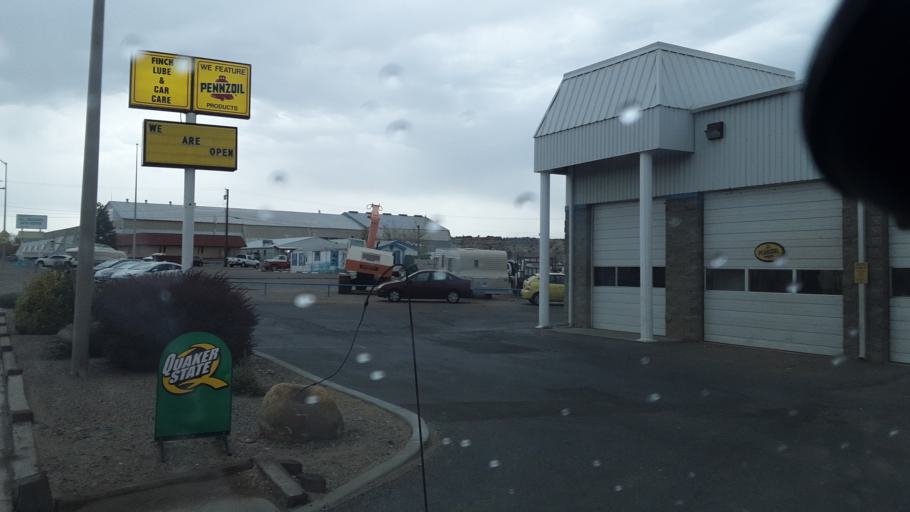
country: US
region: New Mexico
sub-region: San Juan County
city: Farmington
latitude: 36.7383
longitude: -108.1744
